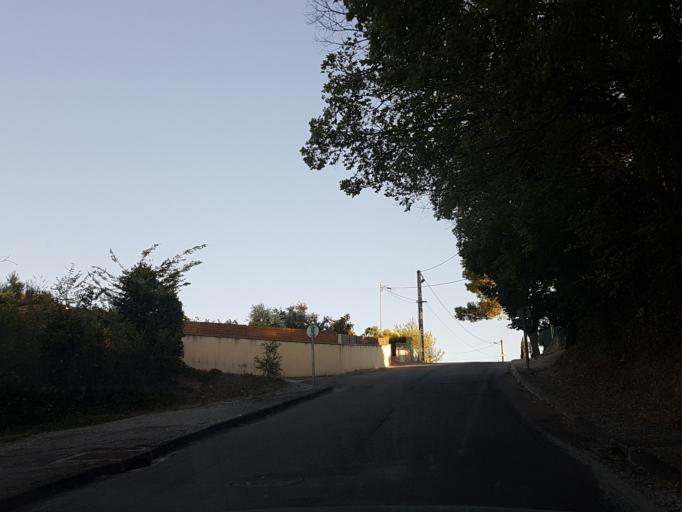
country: FR
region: Provence-Alpes-Cote d'Azur
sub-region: Departement du Vaucluse
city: Pernes-les-Fontaines
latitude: 43.9934
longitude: 5.0607
